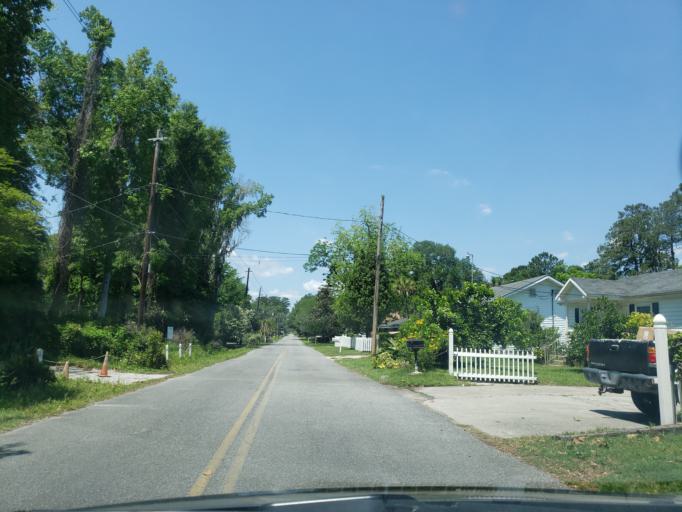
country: US
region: Georgia
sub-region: Chatham County
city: Isle of Hope
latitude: 31.9821
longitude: -81.0619
